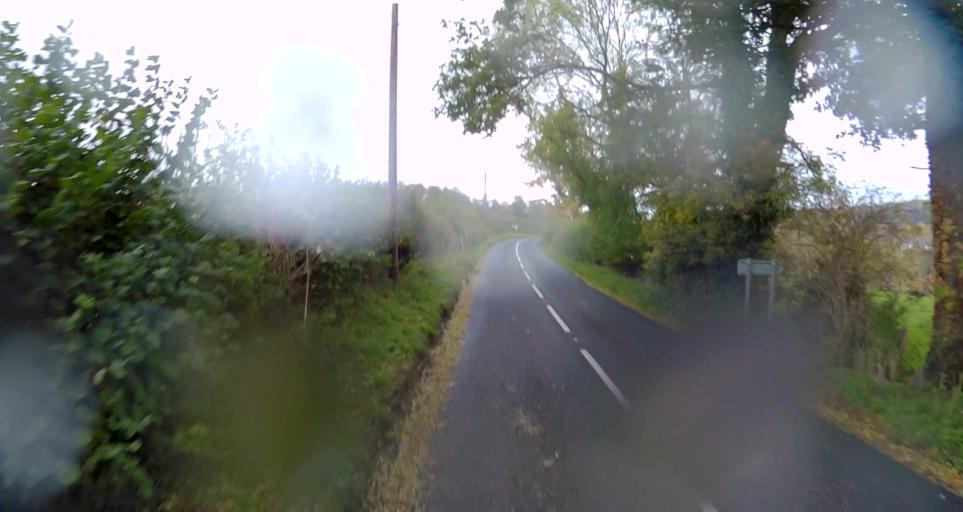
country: GB
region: England
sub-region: Hampshire
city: Kings Worthy
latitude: 51.1361
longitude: -1.1863
